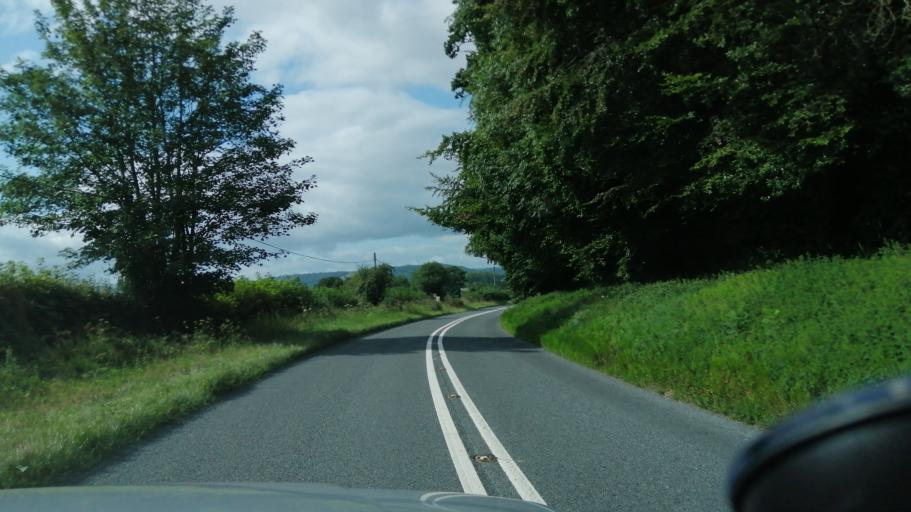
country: GB
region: England
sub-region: Herefordshire
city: Kinnersley
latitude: 52.1401
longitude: -2.9596
